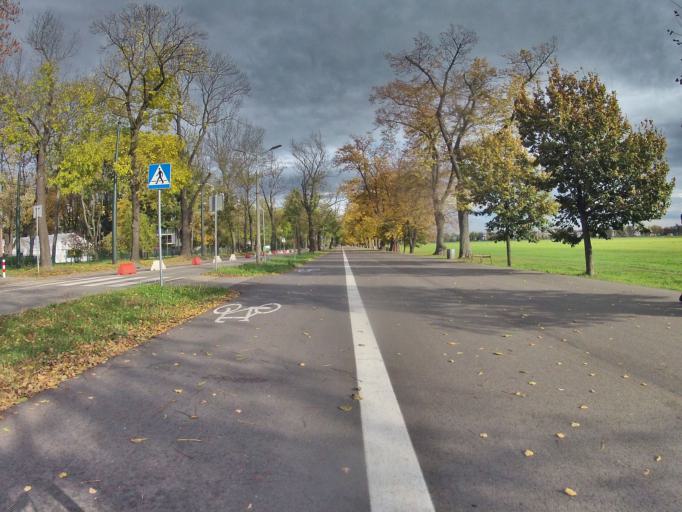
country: PL
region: Lesser Poland Voivodeship
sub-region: Krakow
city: Krakow
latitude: 50.0620
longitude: 19.9055
